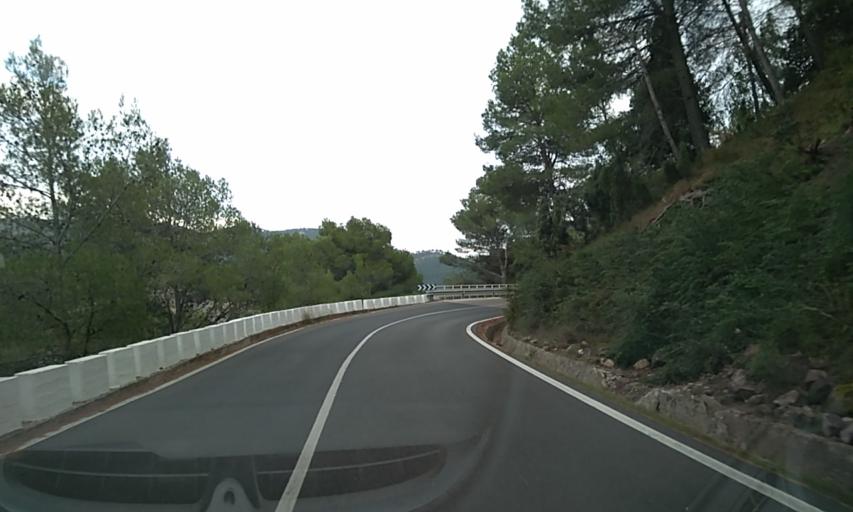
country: ES
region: Valencia
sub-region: Provincia de Castello
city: Puebla de Arenoso
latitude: 40.0863
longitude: -0.5557
